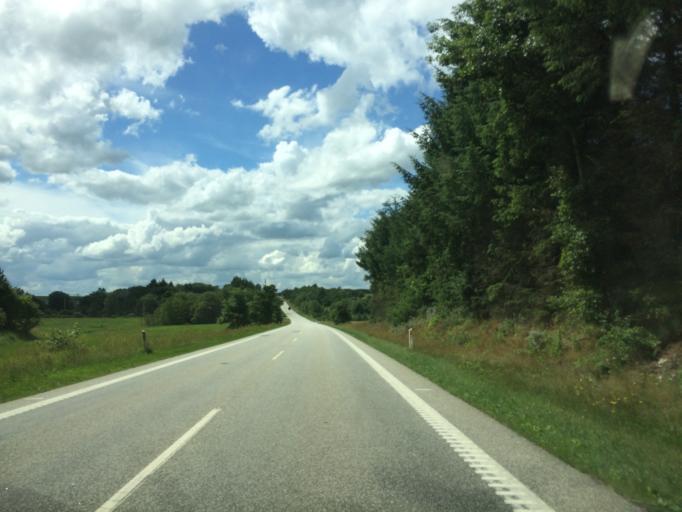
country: DK
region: North Denmark
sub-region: Vesthimmerland Kommune
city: Alestrup
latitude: 56.6225
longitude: 9.5449
